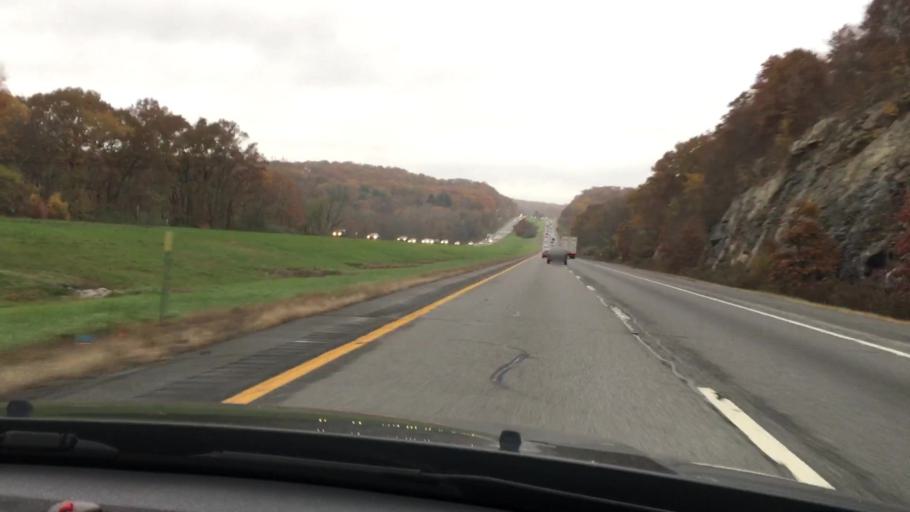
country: US
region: New York
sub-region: Putnam County
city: Brewster Hill
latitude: 41.4451
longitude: -73.6343
